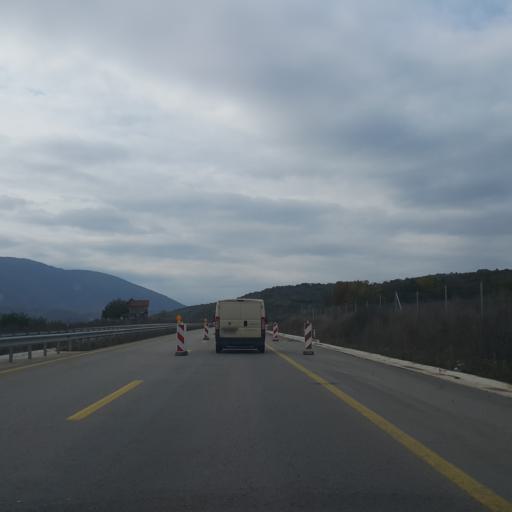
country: RS
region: Central Serbia
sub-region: Pirotski Okrug
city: Bela Palanka
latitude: 43.2370
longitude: 22.3441
